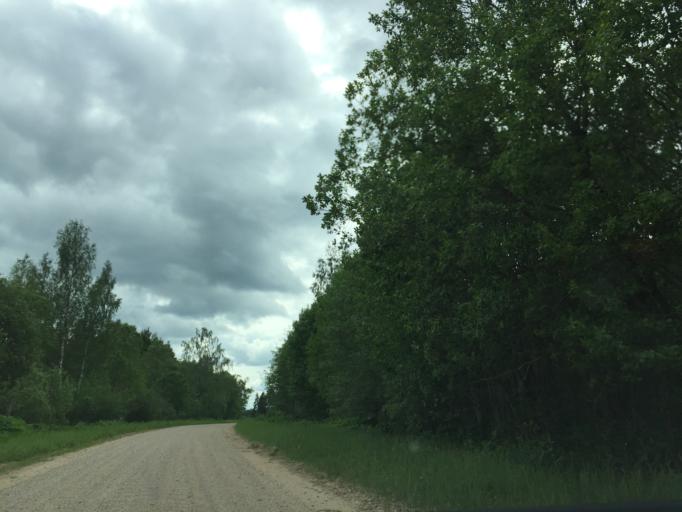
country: LV
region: Dagda
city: Dagda
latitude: 56.0764
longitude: 27.6662
